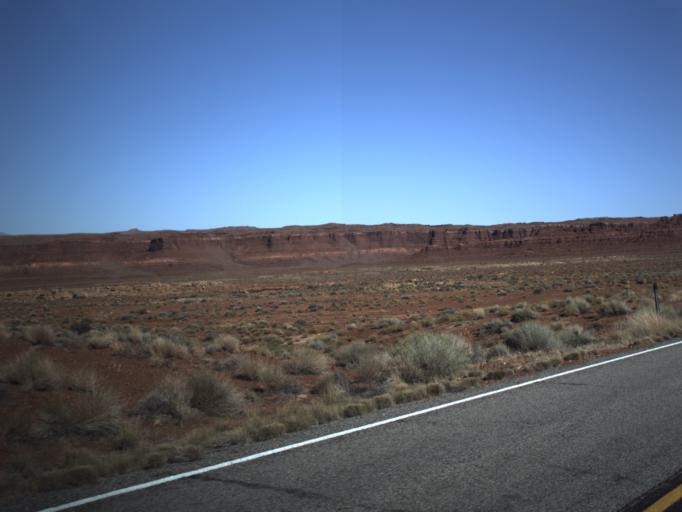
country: US
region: Utah
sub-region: San Juan County
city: Blanding
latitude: 37.8368
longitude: -110.3568
